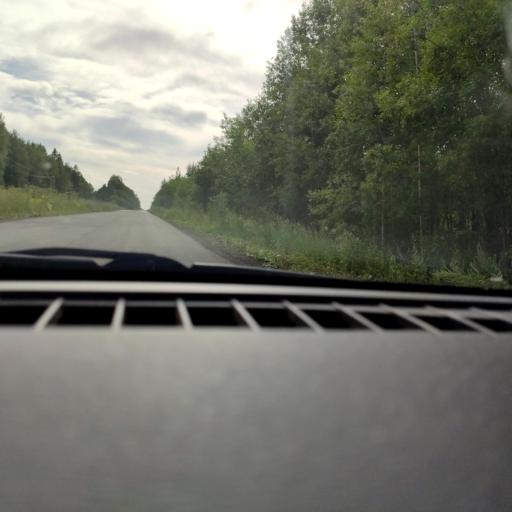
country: RU
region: Perm
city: Polazna
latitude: 58.3373
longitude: 56.1693
